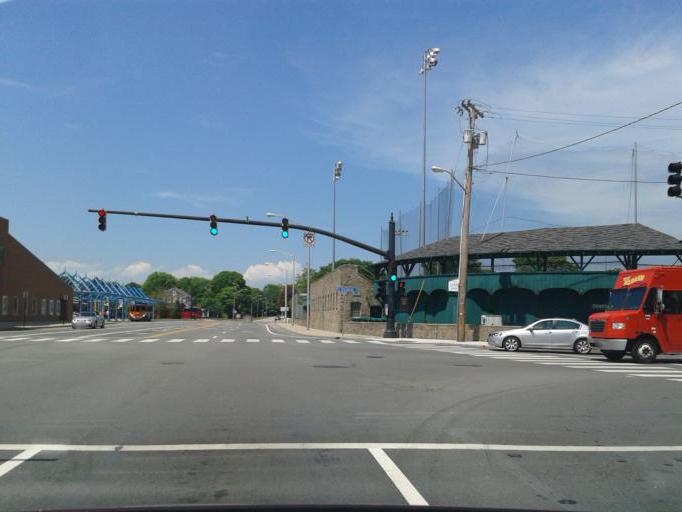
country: US
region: Rhode Island
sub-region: Newport County
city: Newport
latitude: 41.4904
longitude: -71.3171
